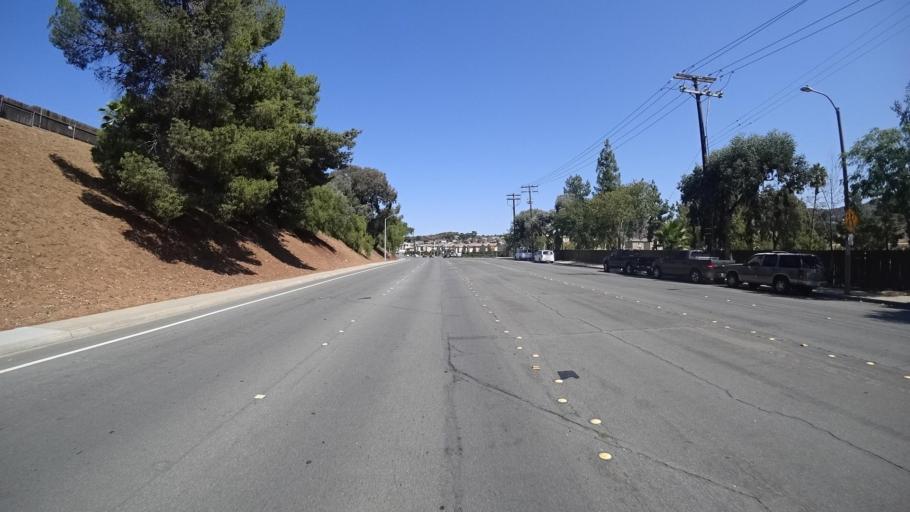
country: US
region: California
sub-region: San Diego County
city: Granite Hills
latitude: 32.8162
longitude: -116.9159
